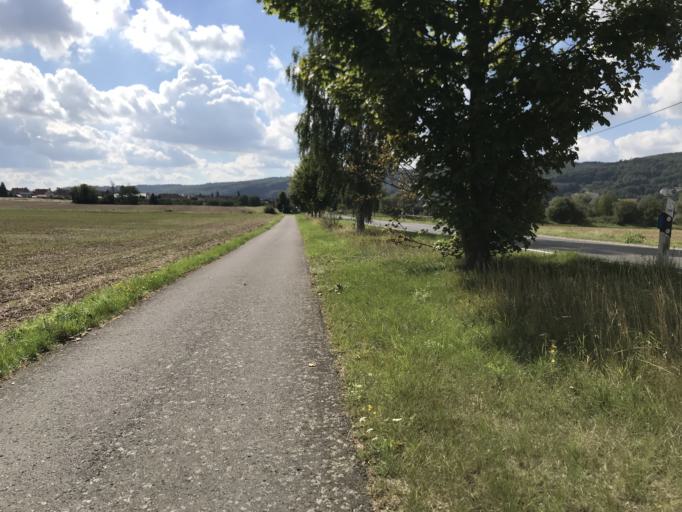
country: DE
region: Hesse
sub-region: Regierungsbezirk Kassel
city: Bad Sooden-Allendorf
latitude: 51.2844
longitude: 9.9751
